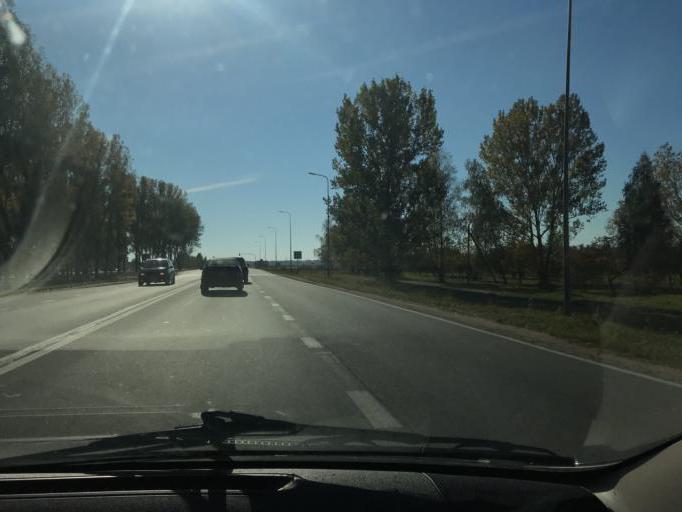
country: BY
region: Minsk
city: Starobin
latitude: 52.7294
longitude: 27.4453
